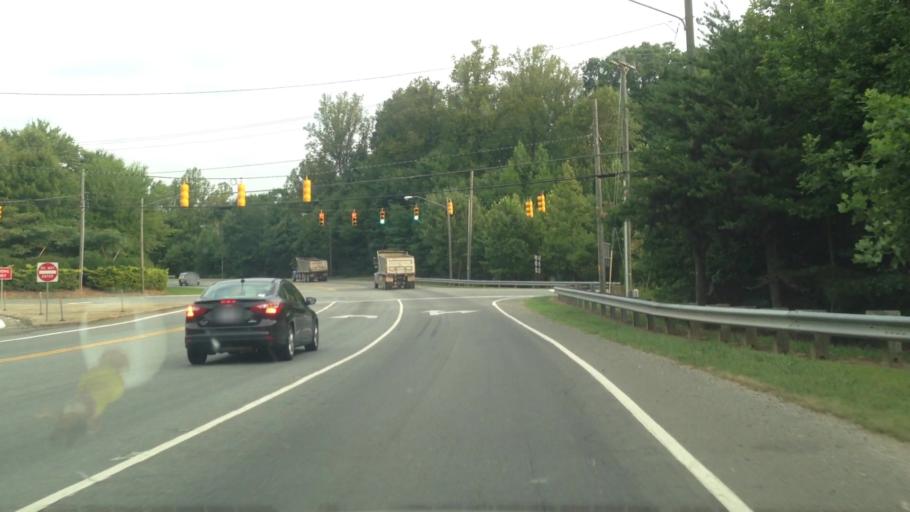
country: US
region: North Carolina
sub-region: Forsyth County
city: Walkertown
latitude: 36.1728
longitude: -80.1654
